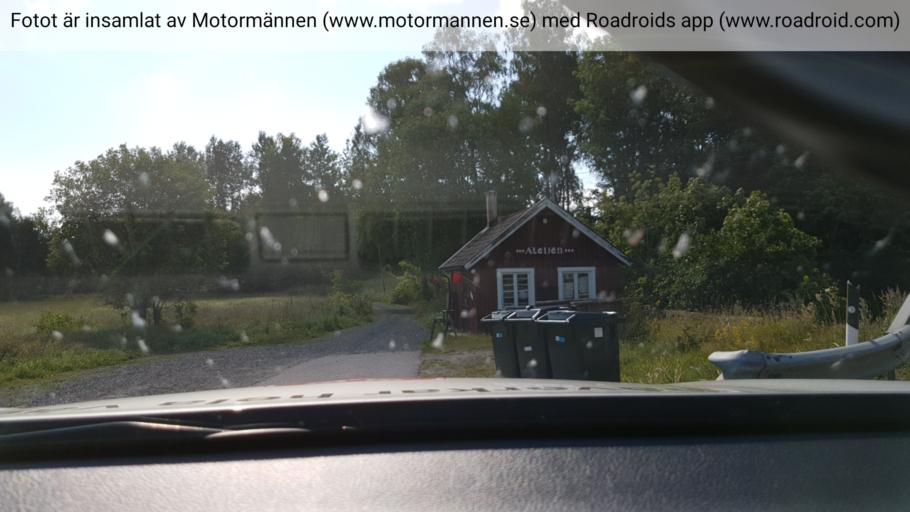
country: SE
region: Stockholm
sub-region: Norrtalje Kommun
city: Norrtalje
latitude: 59.6789
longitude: 18.6835
